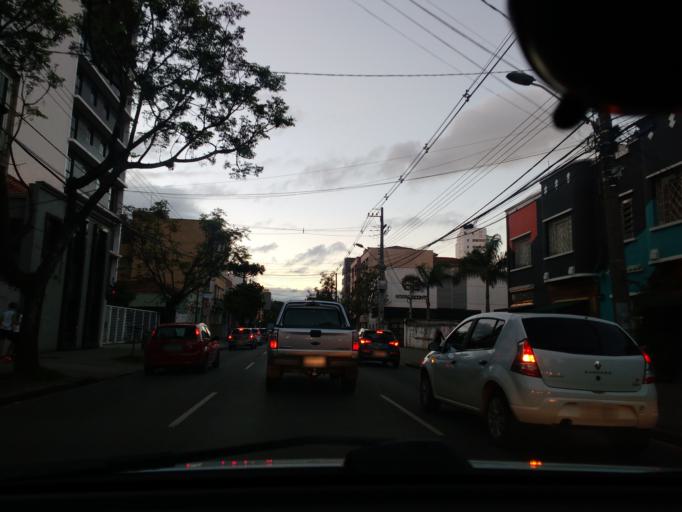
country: BR
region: Parana
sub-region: Curitiba
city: Curitiba
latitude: -25.4324
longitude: -49.2829
